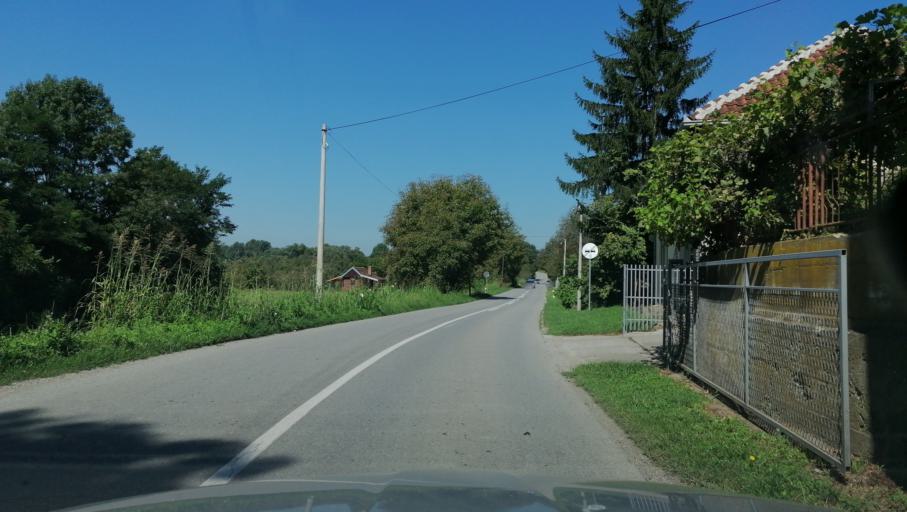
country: RS
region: Central Serbia
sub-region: Raski Okrug
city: Vrnjacka Banja
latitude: 43.6923
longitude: 20.8653
